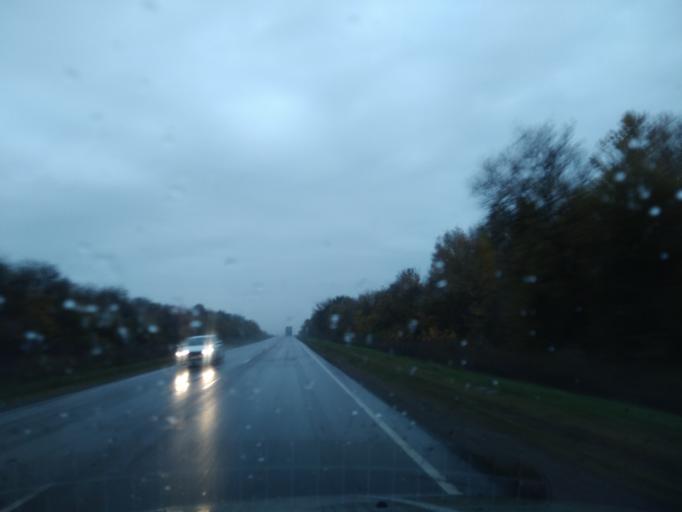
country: RU
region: Tula
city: Yefremov
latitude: 53.1858
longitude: 38.0015
